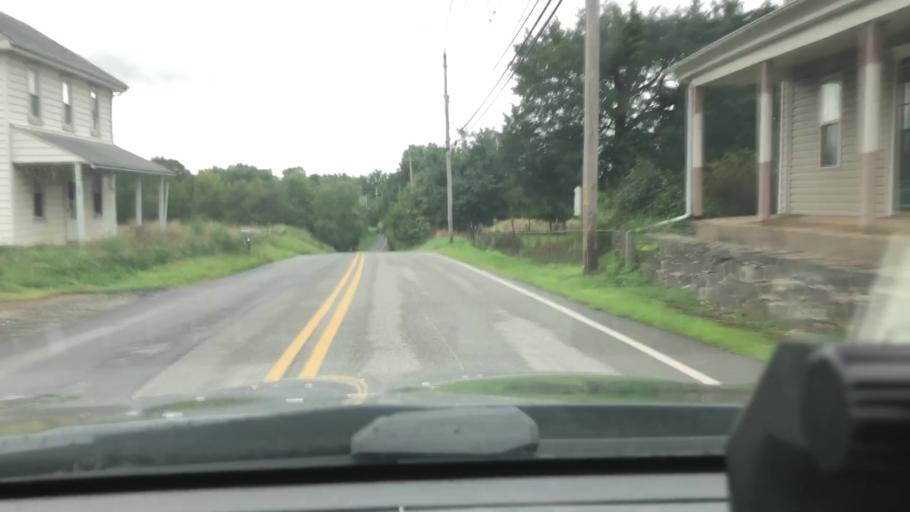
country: US
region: Pennsylvania
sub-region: Montgomery County
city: Gilbertsville
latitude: 40.3087
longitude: -75.6142
